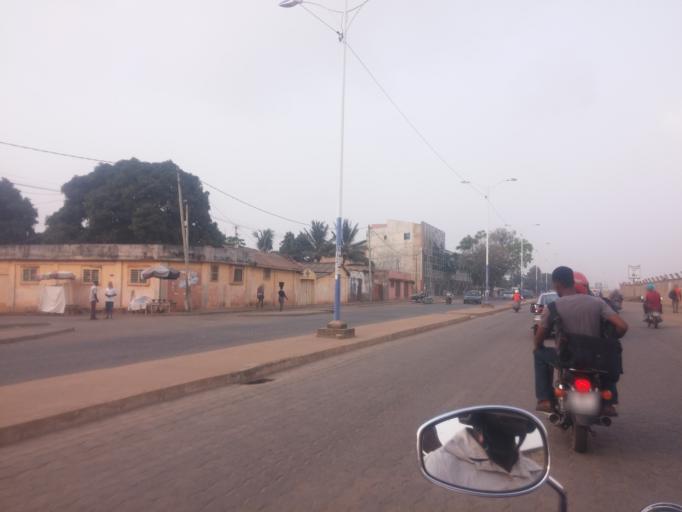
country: TG
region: Maritime
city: Lome
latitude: 6.1553
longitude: 1.2486
